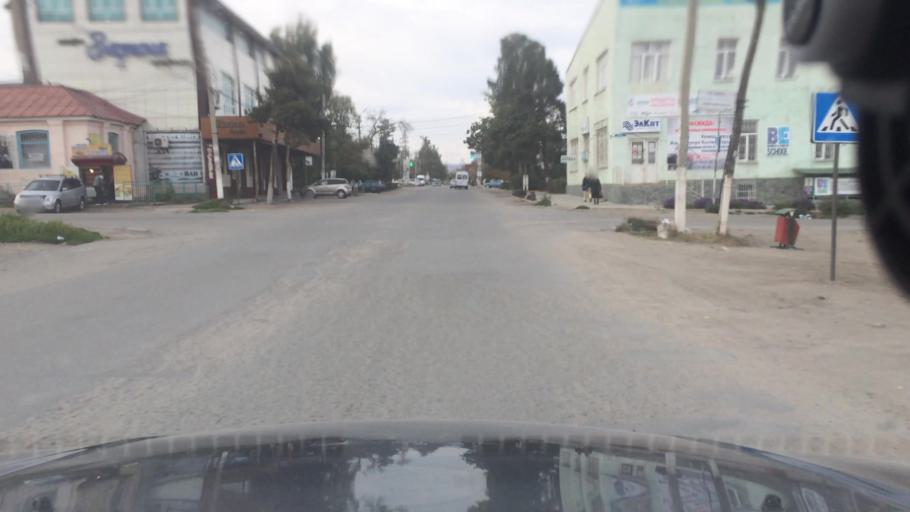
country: KG
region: Ysyk-Koel
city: Karakol
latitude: 42.4906
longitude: 78.3922
